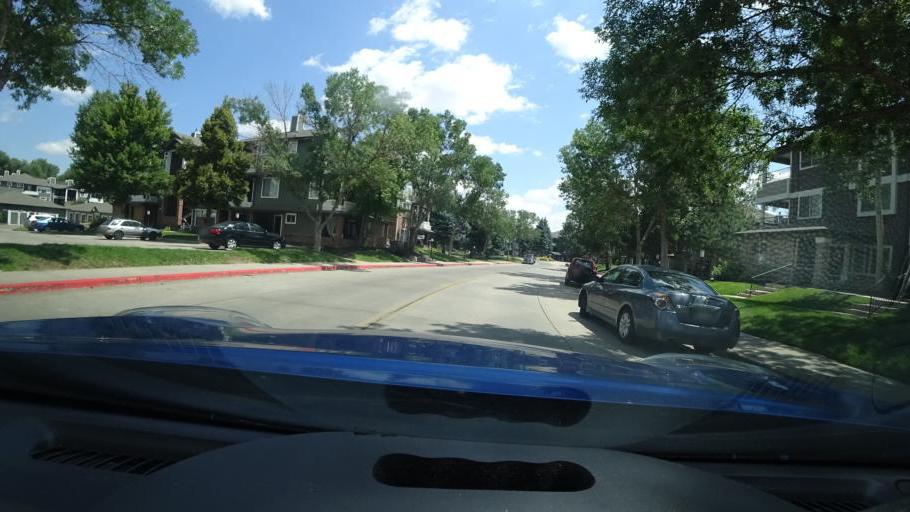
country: US
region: Colorado
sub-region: Arapahoe County
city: Glendale
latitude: 39.6985
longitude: -104.8798
